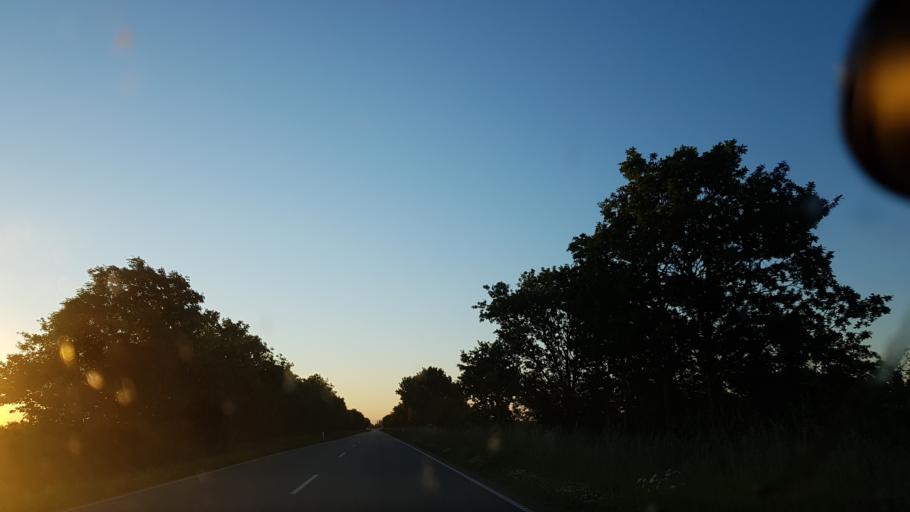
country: DK
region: South Denmark
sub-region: Aabenraa Kommune
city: Krusa
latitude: 54.9279
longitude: 9.3702
